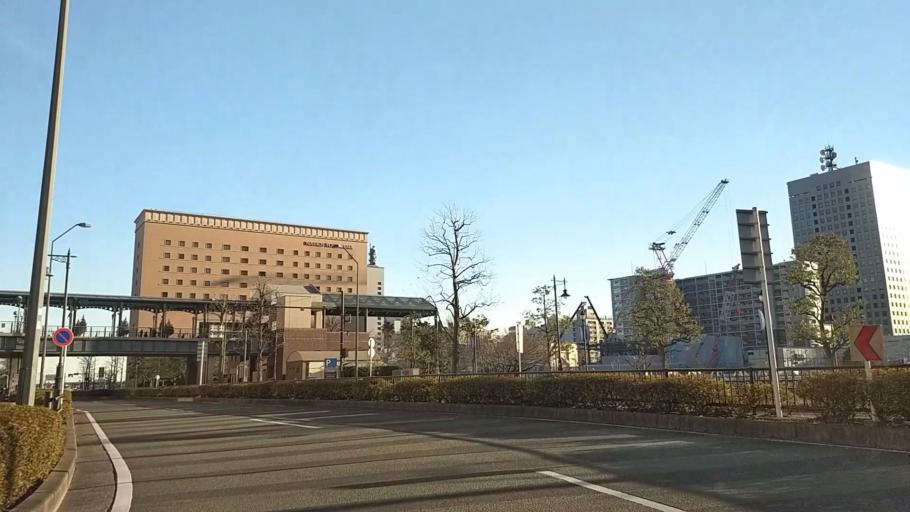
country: JP
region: Kanagawa
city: Yokohama
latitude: 35.4542
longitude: 139.6375
